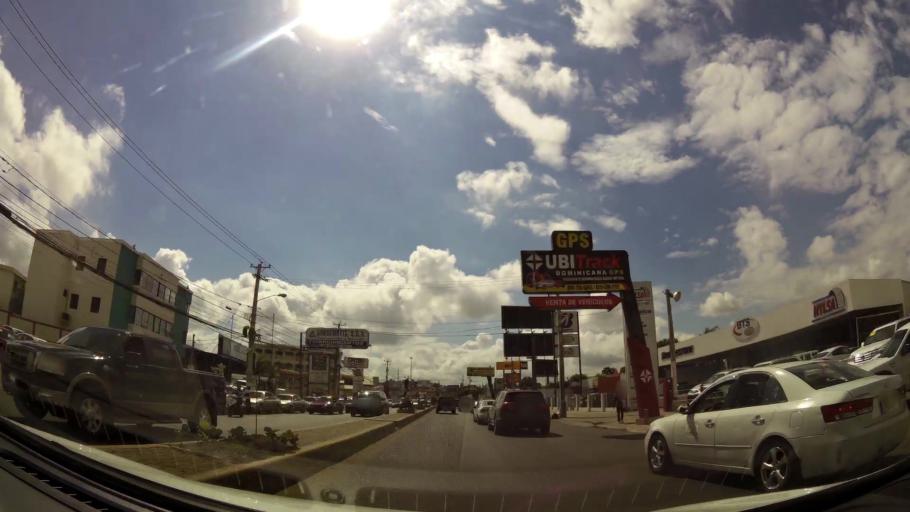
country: DO
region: Santiago
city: Santiago de los Caballeros
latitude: 19.4734
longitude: -70.6936
